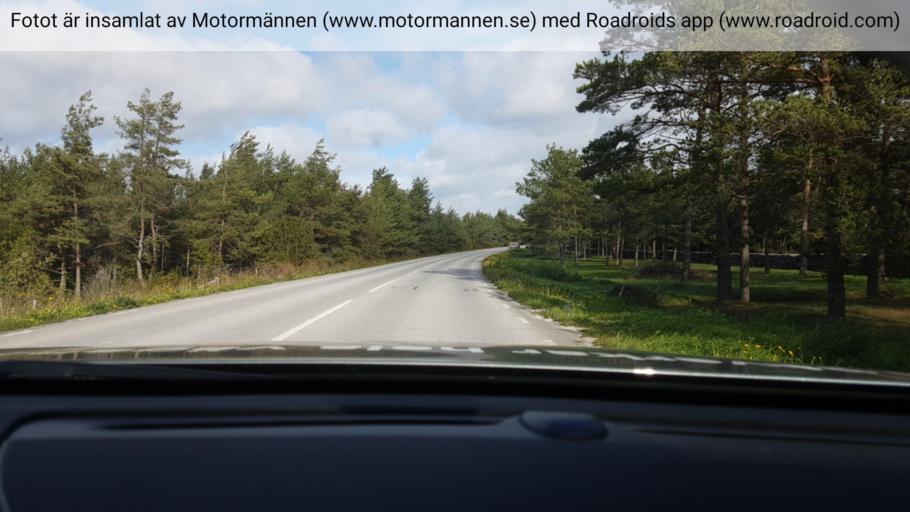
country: SE
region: Gotland
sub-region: Gotland
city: Slite
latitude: 57.8735
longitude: 19.0853
